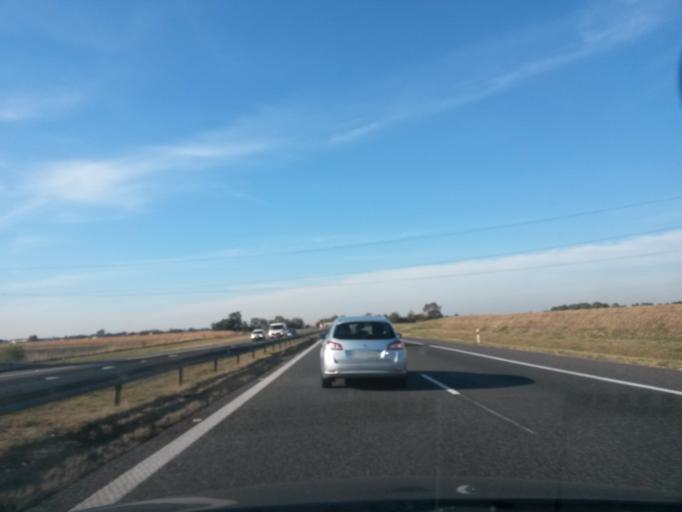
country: PL
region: Lower Silesian Voivodeship
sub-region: Powiat wroclawski
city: Zorawina
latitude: 51.0107
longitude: 17.0284
